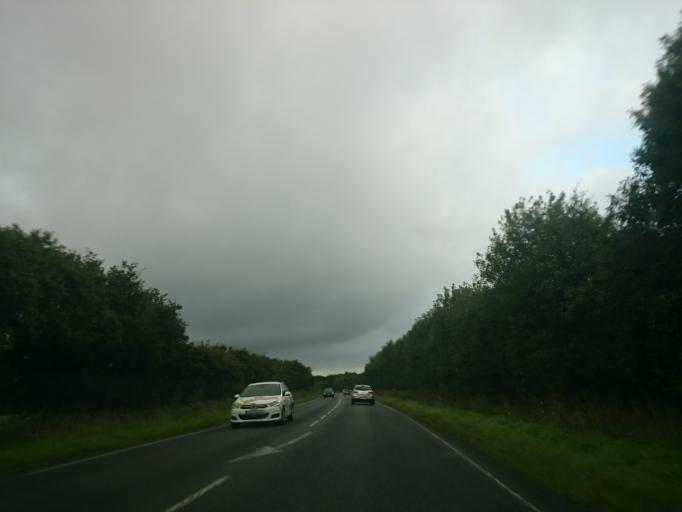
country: FR
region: Brittany
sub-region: Departement du Finistere
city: Gouesnou
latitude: 48.4366
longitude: -4.4477
